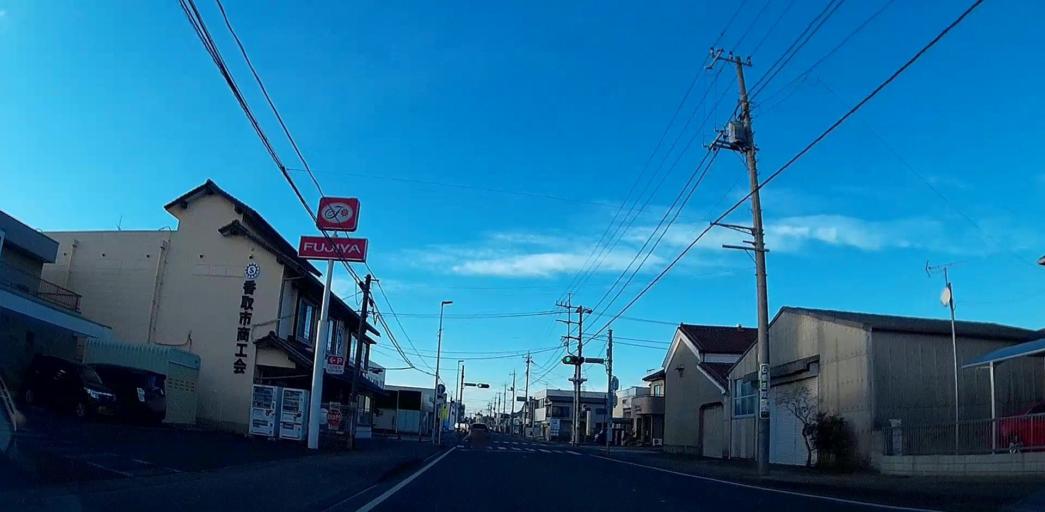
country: JP
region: Chiba
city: Omigawa
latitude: 35.8526
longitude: 140.6084
